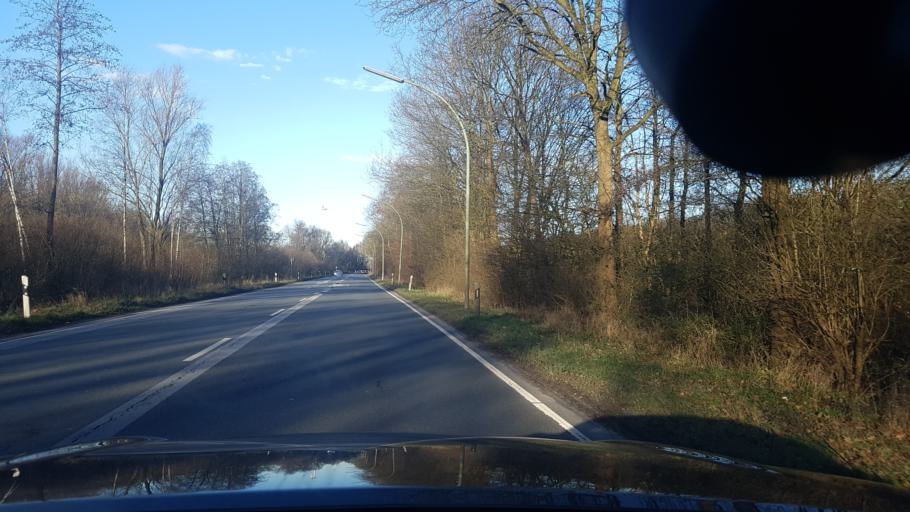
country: DE
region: Bremen
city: Bremerhaven
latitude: 53.5808
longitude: 8.5734
